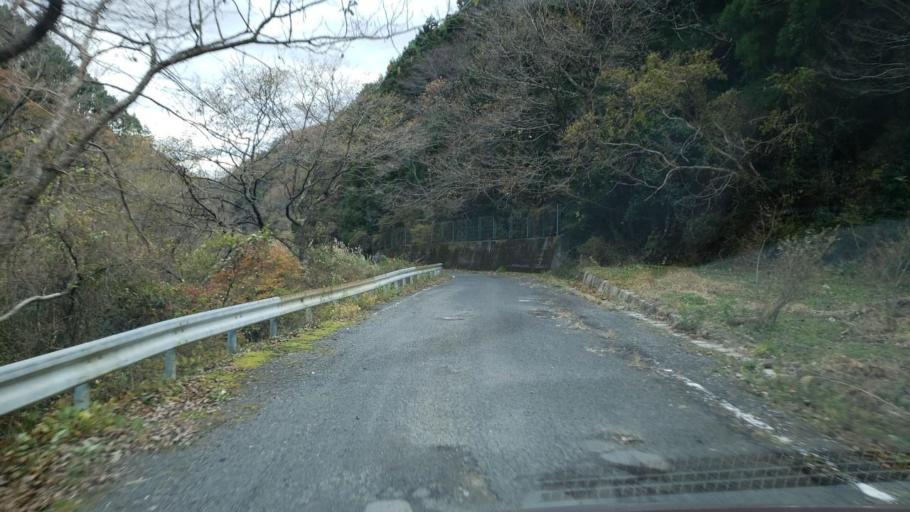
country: JP
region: Tokushima
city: Wakimachi
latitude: 34.1397
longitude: 134.2304
